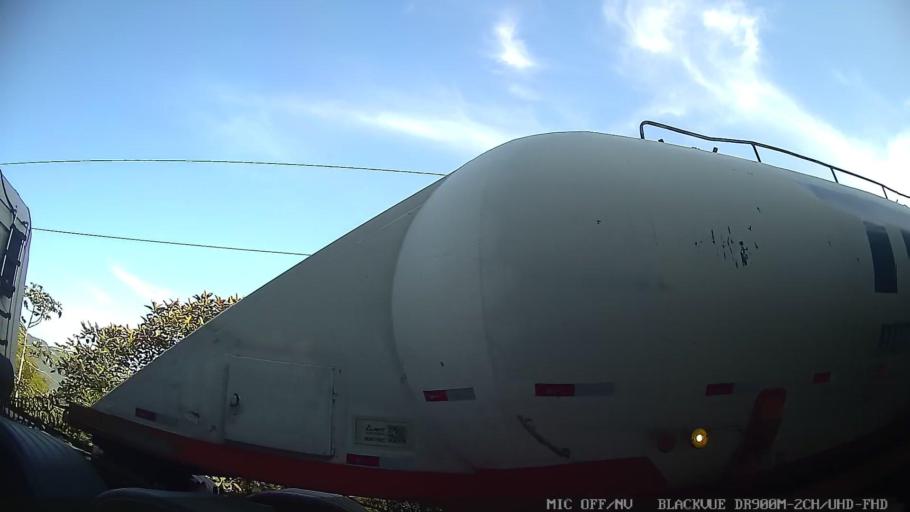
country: BR
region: Sao Paulo
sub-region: Cubatao
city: Cubatao
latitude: -23.8803
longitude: -46.4882
